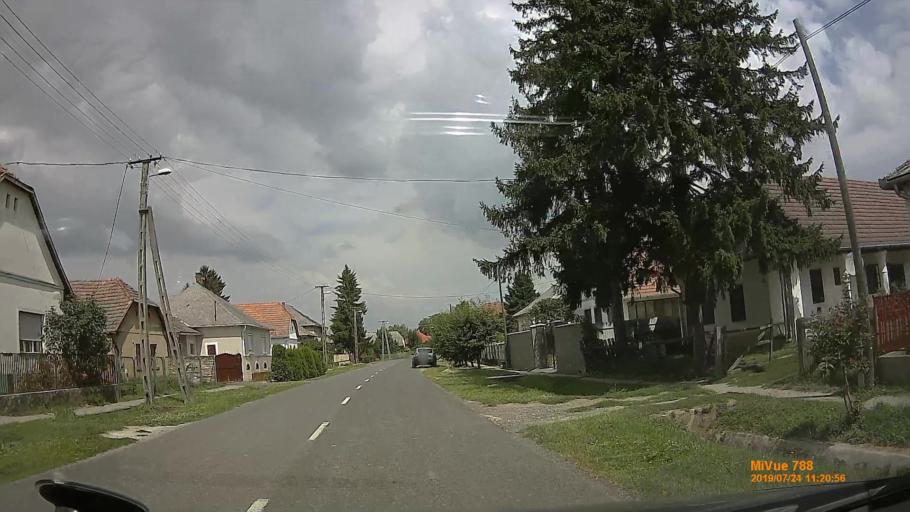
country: HU
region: Szabolcs-Szatmar-Bereg
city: Tarpa
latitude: 48.1622
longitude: 22.4582
